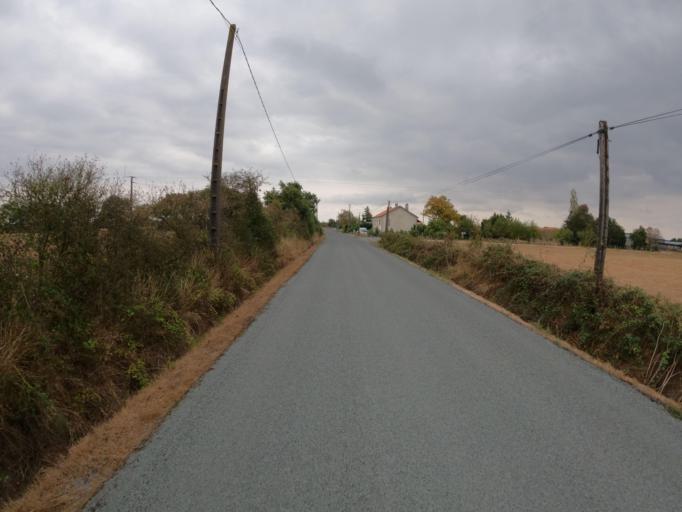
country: FR
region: Pays de la Loire
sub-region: Departement de la Vendee
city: Treize-Septiers
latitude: 46.9793
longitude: -1.2127
